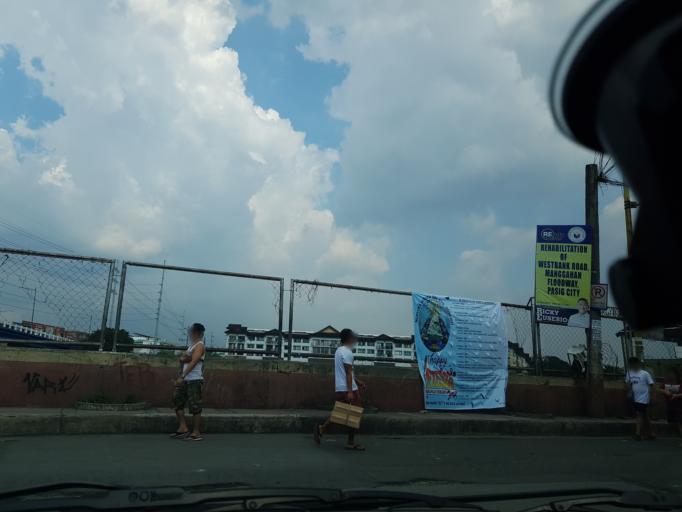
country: PH
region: Metro Manila
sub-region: Pasig
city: Pasig City
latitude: 14.5895
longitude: 121.0922
